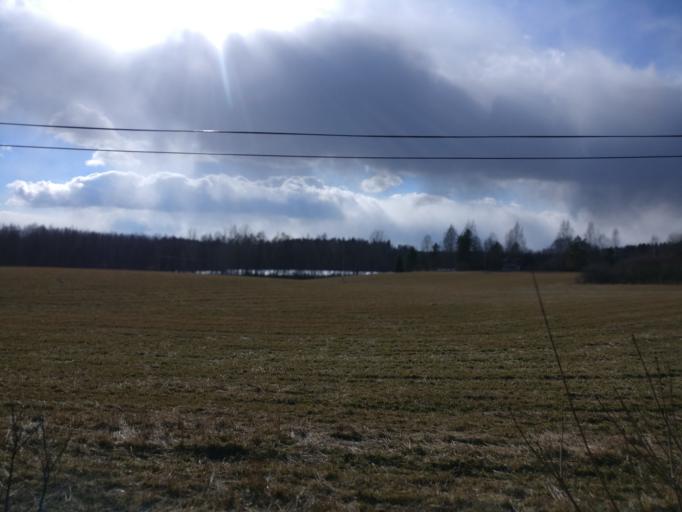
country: FI
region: Uusimaa
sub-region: Helsinki
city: Karjalohja
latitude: 60.2686
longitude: 23.6667
